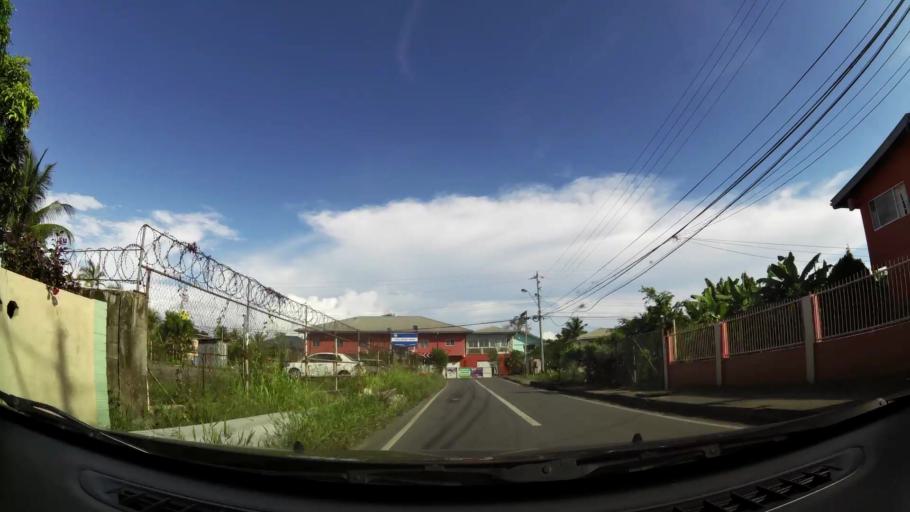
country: TT
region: Chaguanas
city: Chaguanas
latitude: 10.5321
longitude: -61.3792
